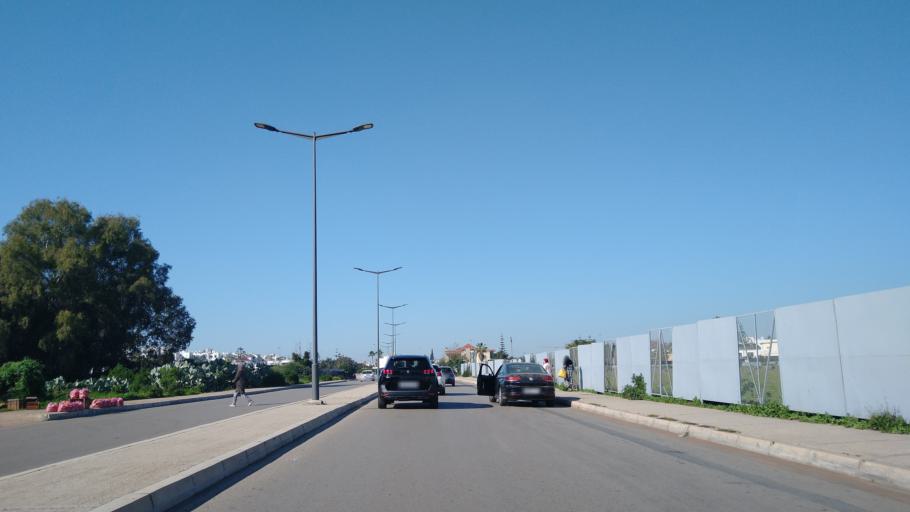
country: MA
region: Rabat-Sale-Zemmour-Zaer
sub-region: Skhirate-Temara
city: Temara
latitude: 33.9541
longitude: -6.8561
